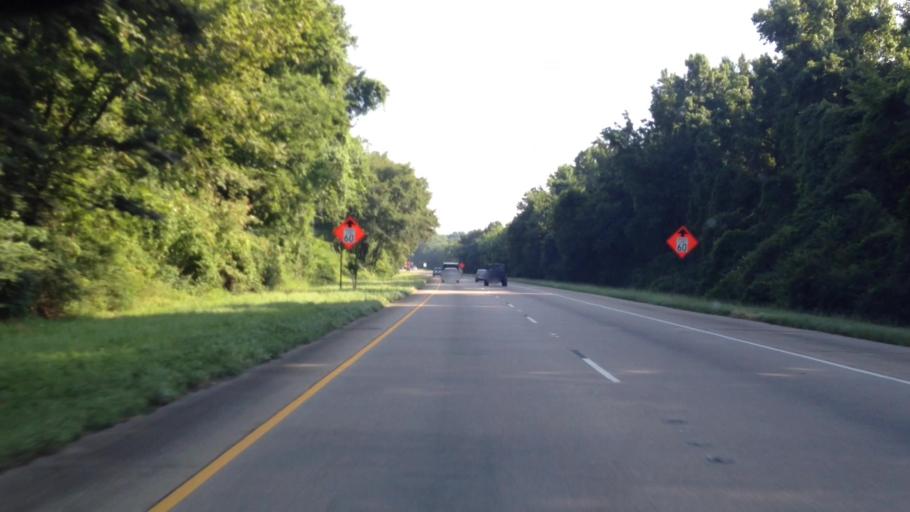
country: US
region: Louisiana
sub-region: Ascension Parish
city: Prairieville
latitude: 30.3017
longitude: -90.9925
